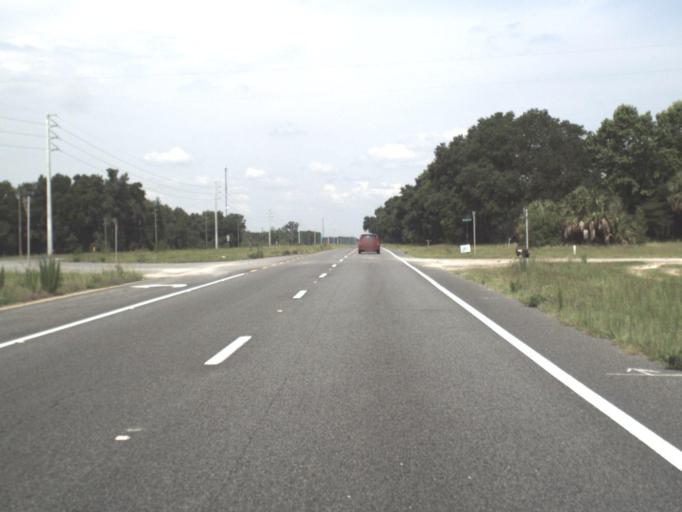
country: US
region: Florida
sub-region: Levy County
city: Chiefland
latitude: 29.4752
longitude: -82.7557
